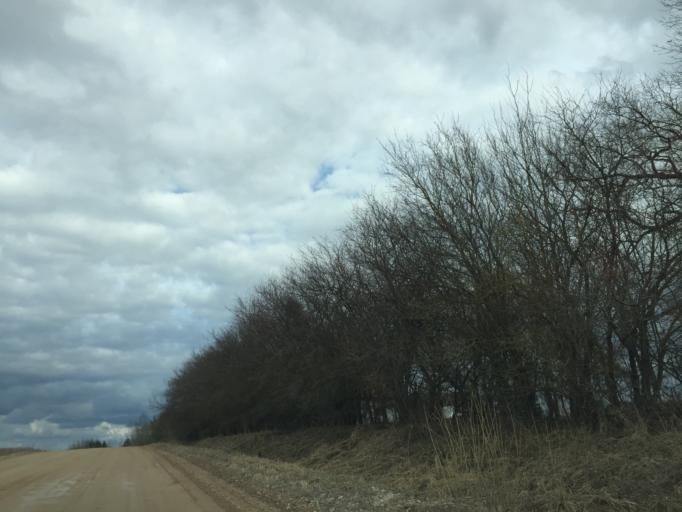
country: LV
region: Lielvarde
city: Lielvarde
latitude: 56.5147
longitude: 24.7444
